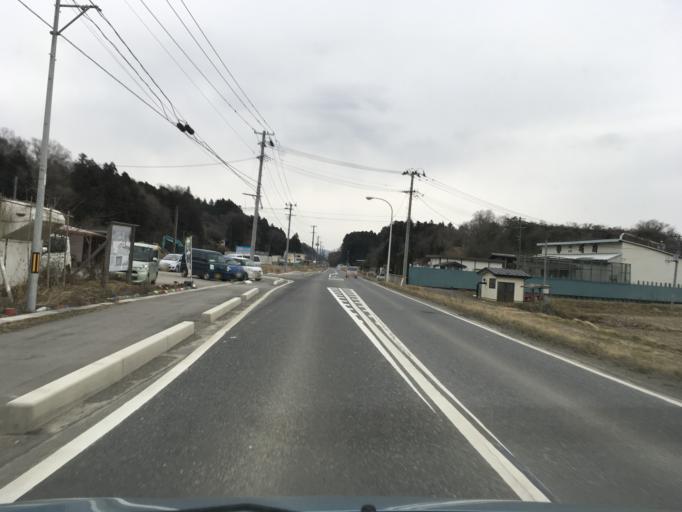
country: JP
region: Miyagi
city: Wakuya
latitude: 38.6711
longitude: 141.2715
